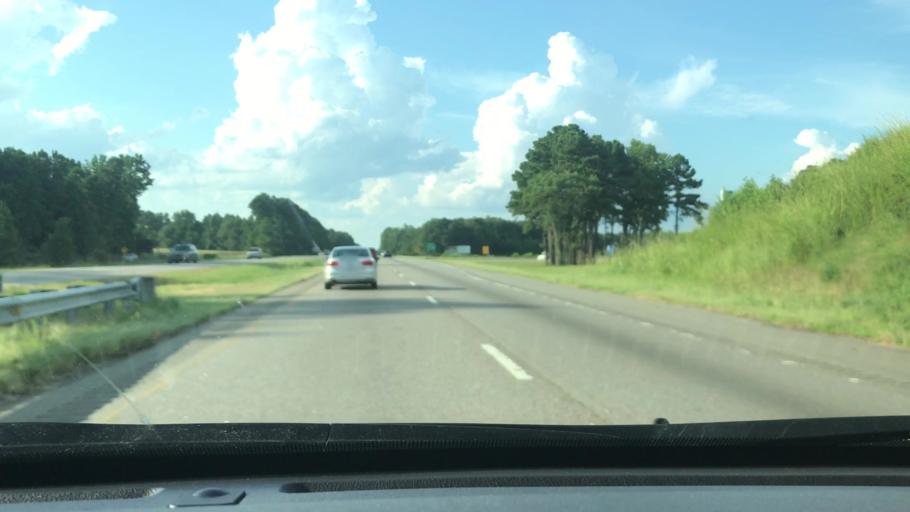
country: US
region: North Carolina
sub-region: Robeson County
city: Saint Pauls
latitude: 34.7202
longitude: -78.9973
